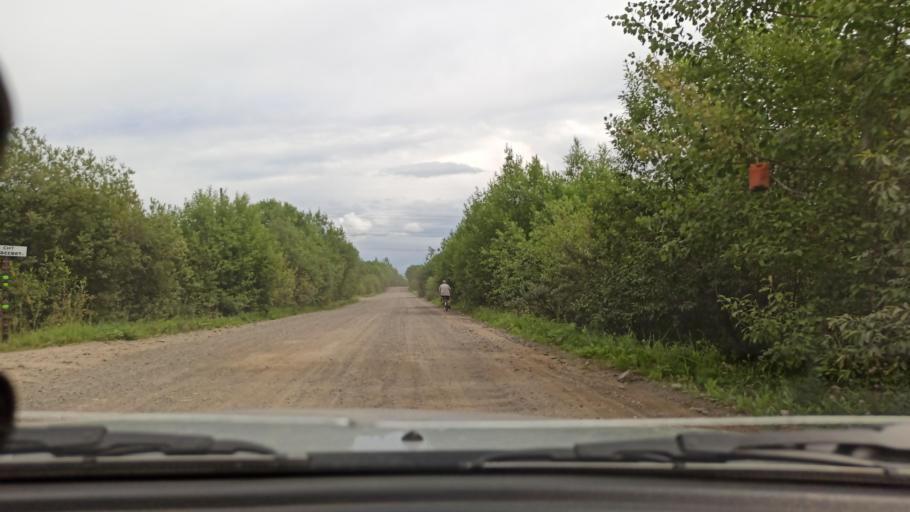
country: RU
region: Vologda
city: Molochnoye
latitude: 59.3693
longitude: 39.6817
